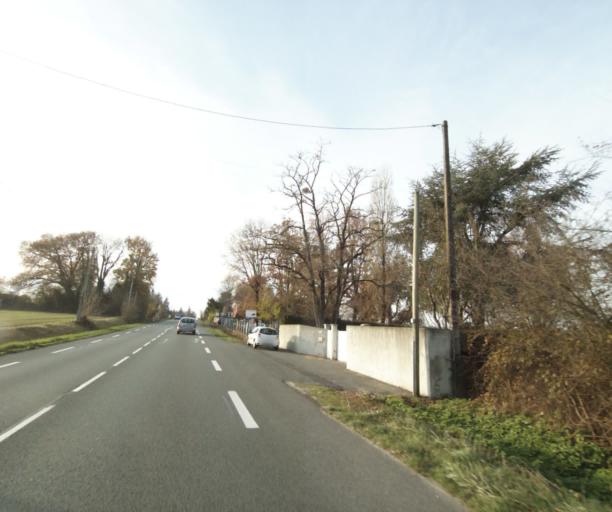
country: FR
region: Poitou-Charentes
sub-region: Departement de la Charente-Maritime
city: Fontcouverte
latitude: 45.7454
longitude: -0.5819
